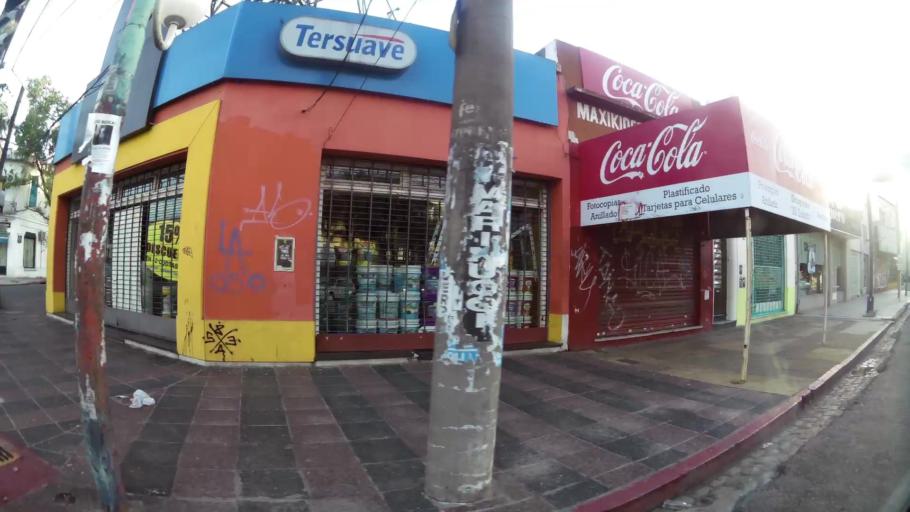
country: AR
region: Buenos Aires
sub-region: Partido de Moron
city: Moron
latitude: -34.6493
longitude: -58.6142
